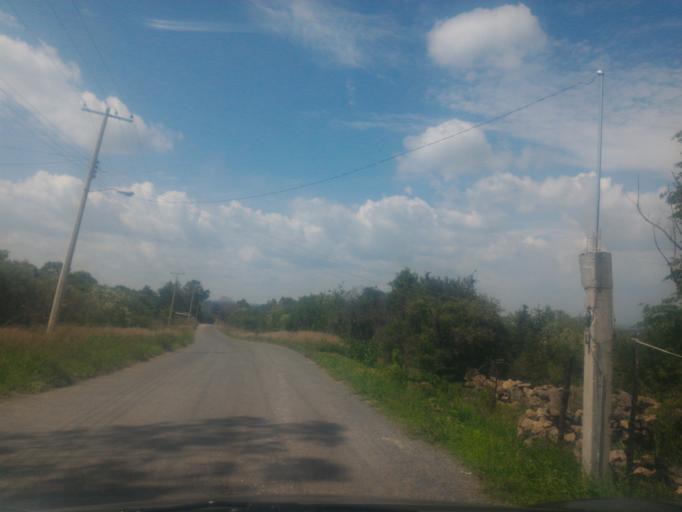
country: MX
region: Guanajuato
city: Ciudad Manuel Doblado
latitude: 20.8227
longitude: -102.0587
